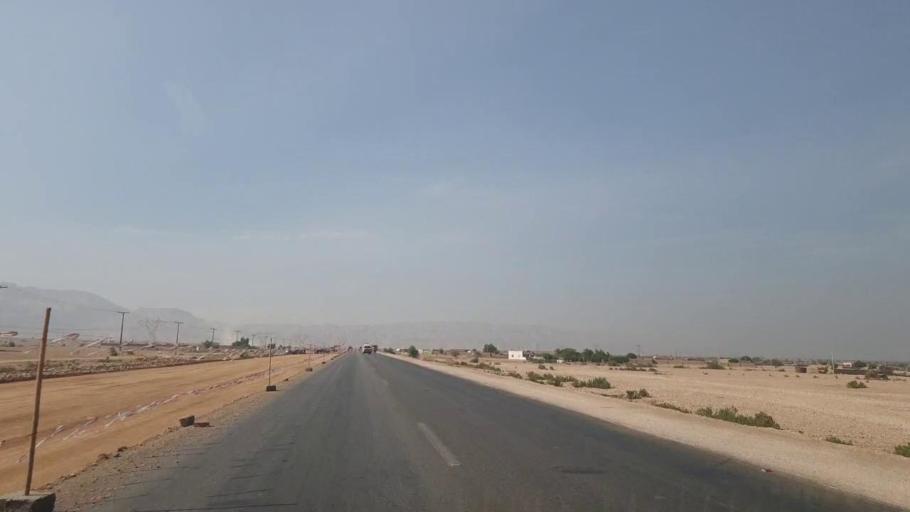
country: PK
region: Sindh
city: Sehwan
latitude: 26.1998
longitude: 67.9395
